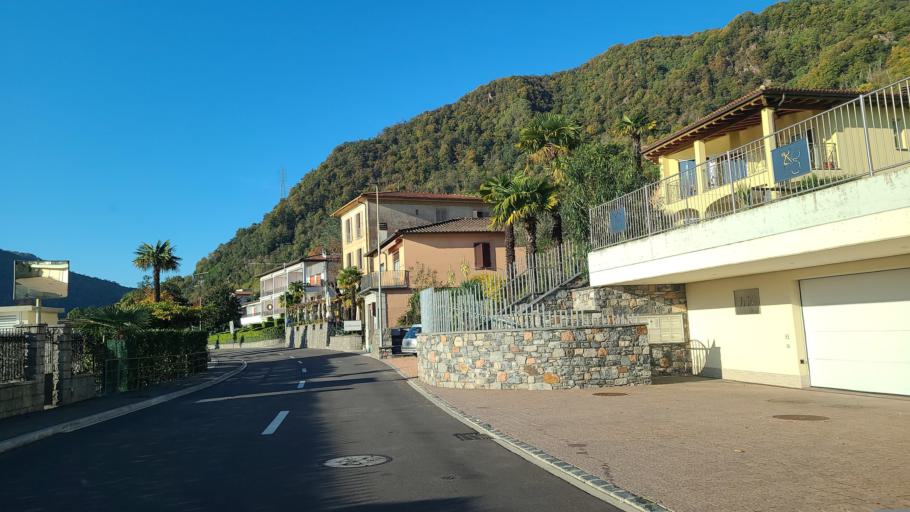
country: IT
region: Lombardy
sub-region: Provincia di Varese
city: Porto Ceresio
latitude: 45.9267
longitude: 8.9078
